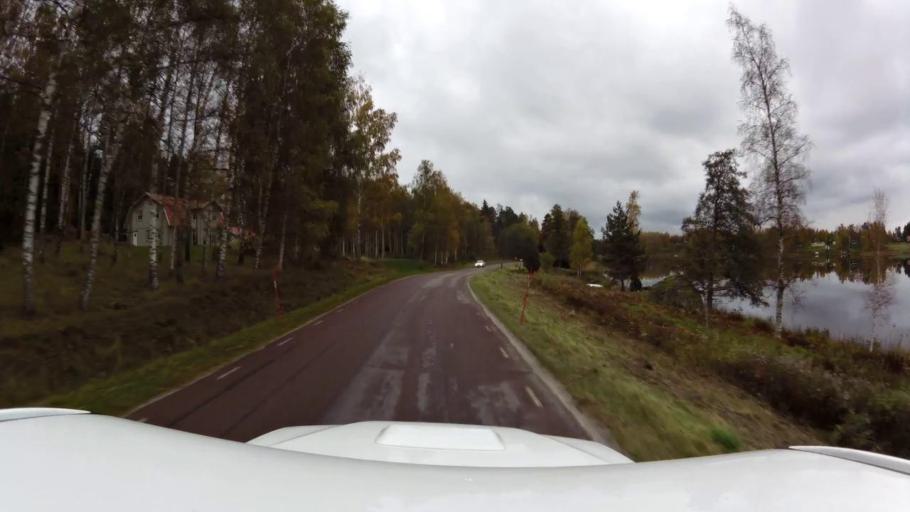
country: SE
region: OEstergoetland
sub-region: Linkopings Kommun
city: Ljungsbro
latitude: 58.5735
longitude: 15.5120
